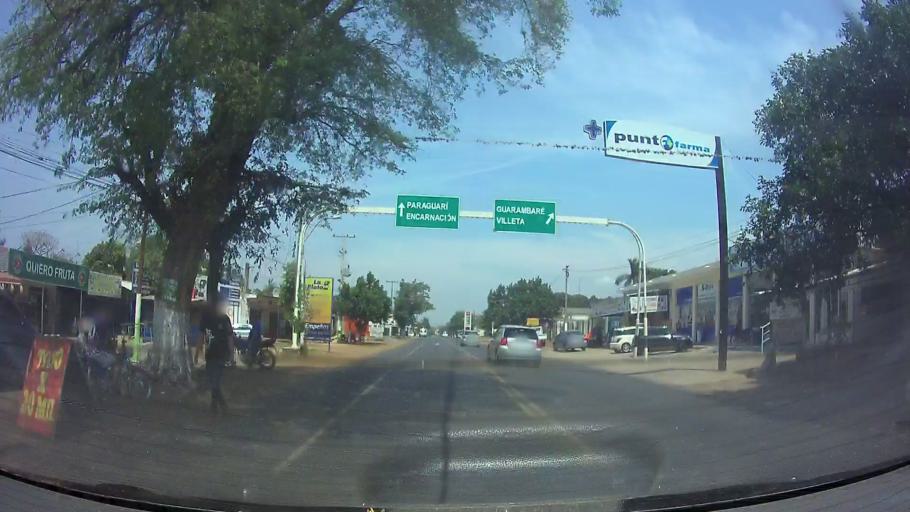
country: PY
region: Central
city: Guarambare
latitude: -25.4451
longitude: -57.4397
